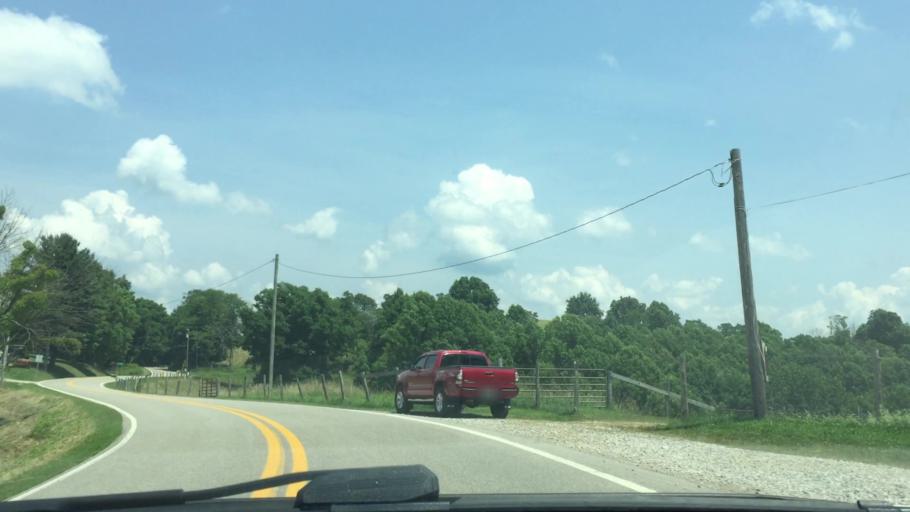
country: US
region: West Virginia
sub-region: Wetzel County
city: New Martinsville
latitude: 39.7016
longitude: -80.7461
